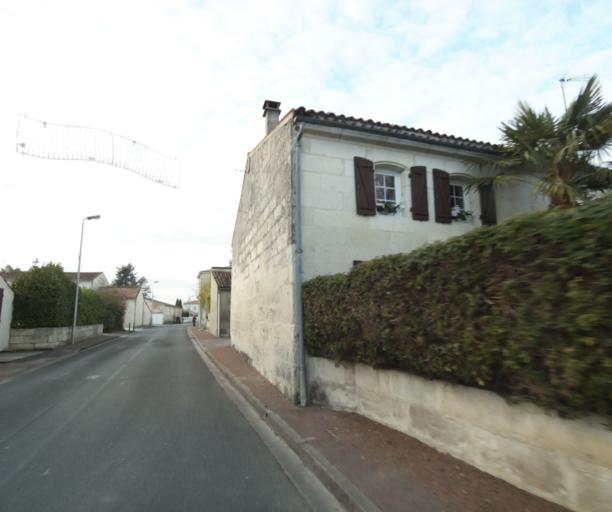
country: FR
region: Poitou-Charentes
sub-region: Departement de la Charente-Maritime
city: Les Gonds
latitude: 45.7136
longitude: -0.6127
